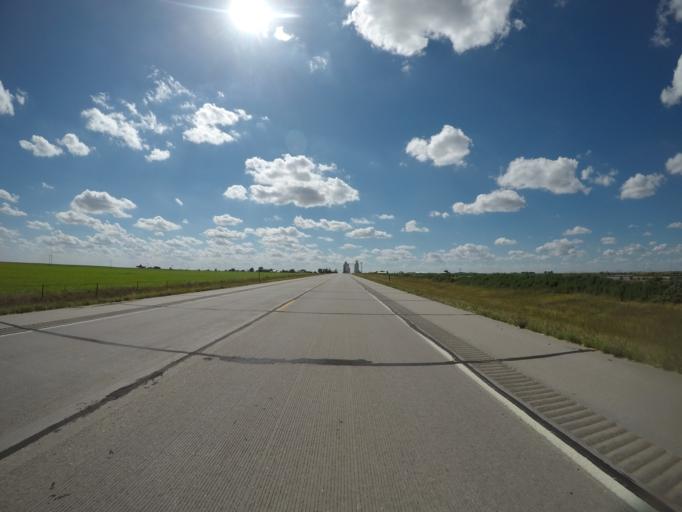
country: US
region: Colorado
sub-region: Phillips County
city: Holyoke
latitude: 40.6106
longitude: -102.4597
